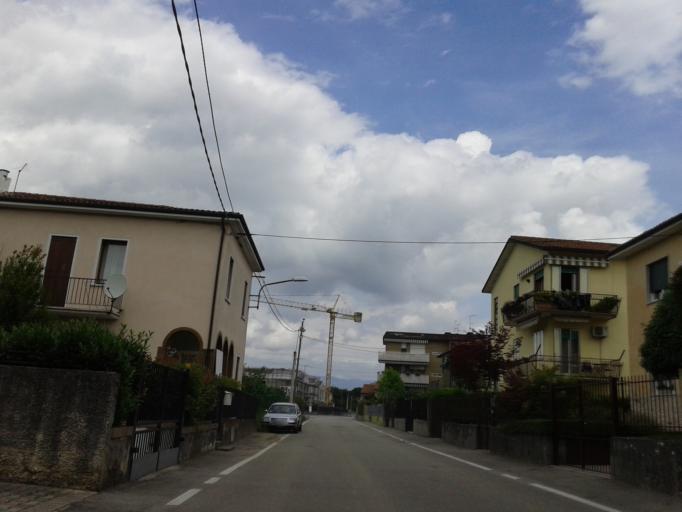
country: IT
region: Veneto
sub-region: Provincia di Vicenza
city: Monticello Conte Otto
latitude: 45.5919
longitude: 11.5517
